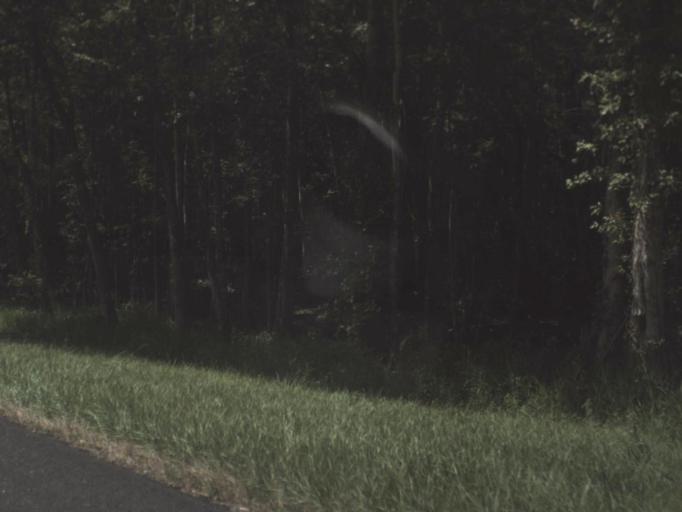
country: US
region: Florida
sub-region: Taylor County
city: Perry
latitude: 30.2270
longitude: -83.6791
